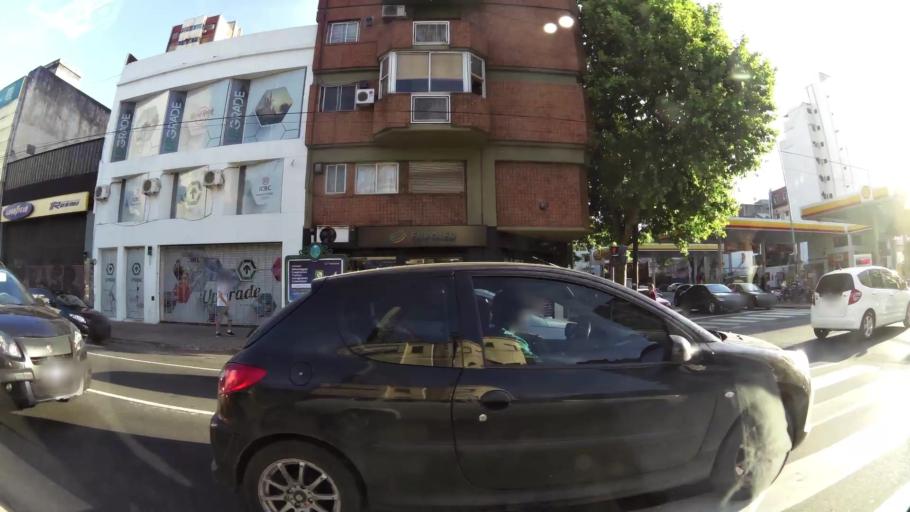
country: AR
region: Buenos Aires F.D.
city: Retiro
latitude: -34.5979
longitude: -58.4189
